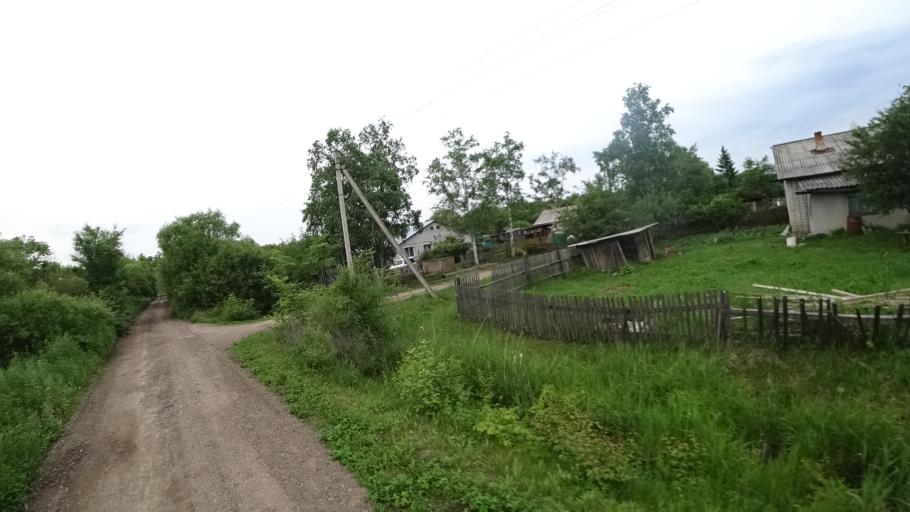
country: RU
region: Primorskiy
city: Novosysoyevka
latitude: 44.2442
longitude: 133.3746
